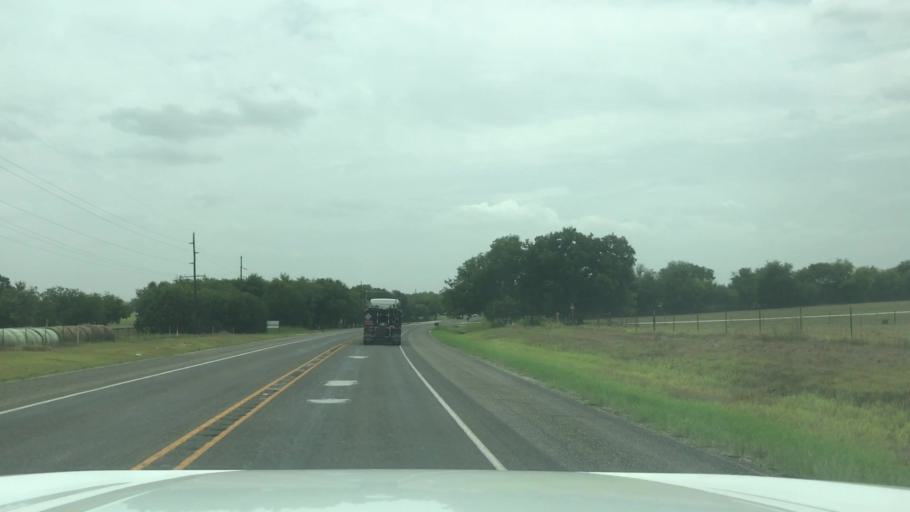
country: US
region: Texas
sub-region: Bosque County
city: Clifton
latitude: 31.7475
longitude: -97.5544
